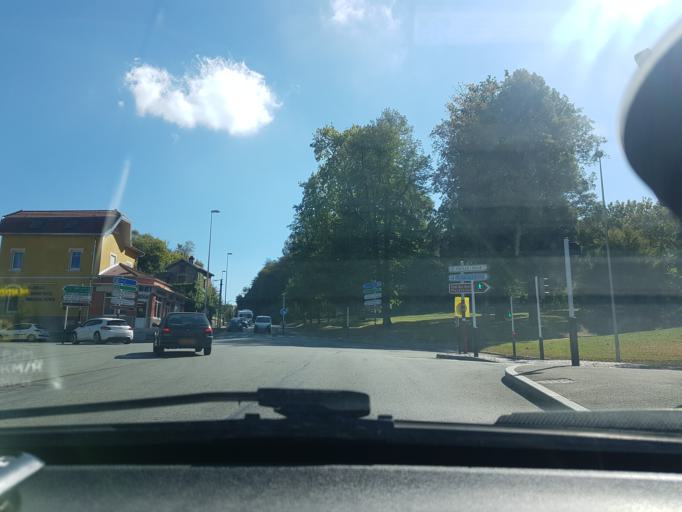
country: FR
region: Franche-Comte
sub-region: Territoire de Belfort
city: Belfort
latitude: 47.6403
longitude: 6.8675
